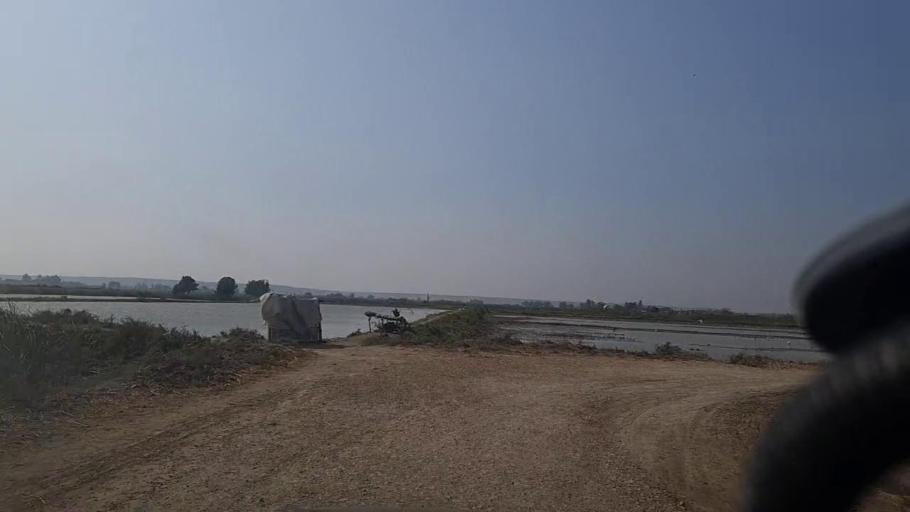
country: PK
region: Sindh
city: Thatta
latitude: 24.6156
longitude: 67.8856
